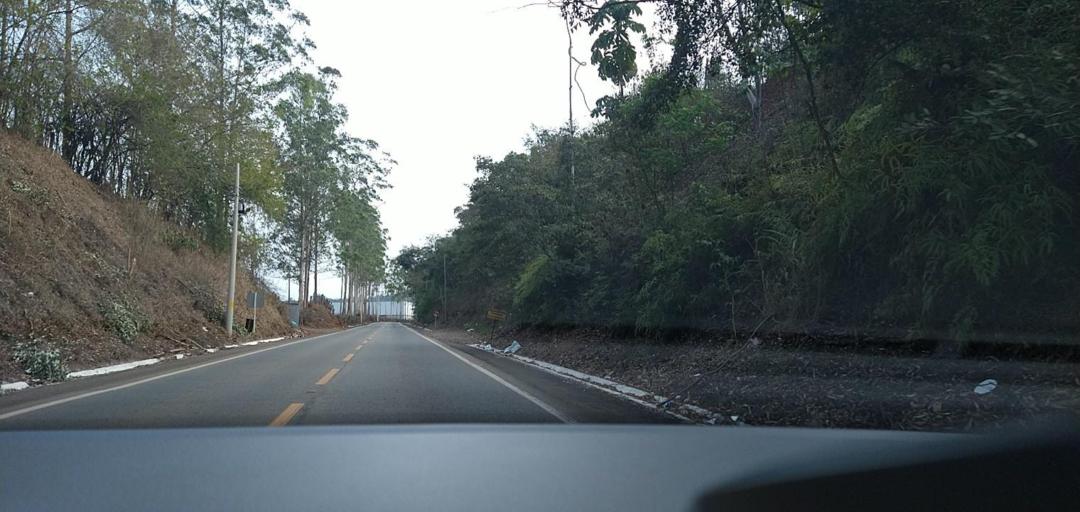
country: BR
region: Minas Gerais
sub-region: Rio Piracicaba
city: Rio Piracicaba
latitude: -19.8828
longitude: -43.1292
